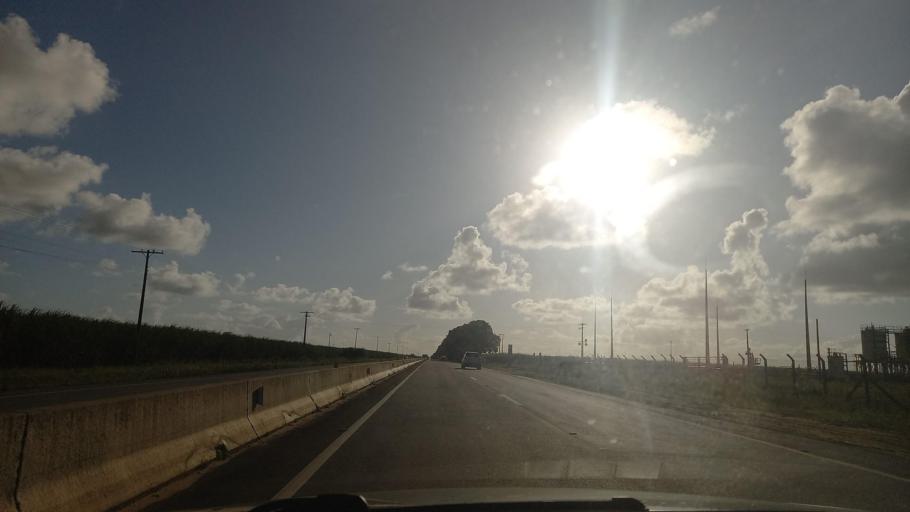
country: BR
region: Alagoas
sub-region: Sao Miguel Dos Campos
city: Sao Miguel dos Campos
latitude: -9.8057
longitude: -36.1254
